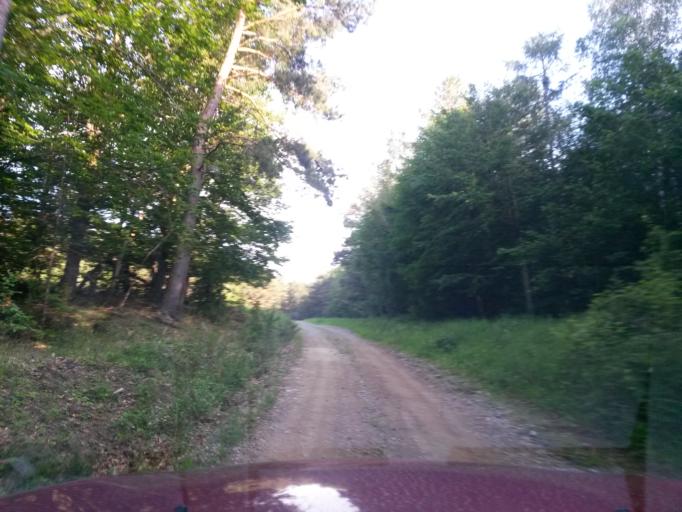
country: SK
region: Kosicky
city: Moldava nad Bodvou
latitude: 48.7437
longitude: 21.0274
